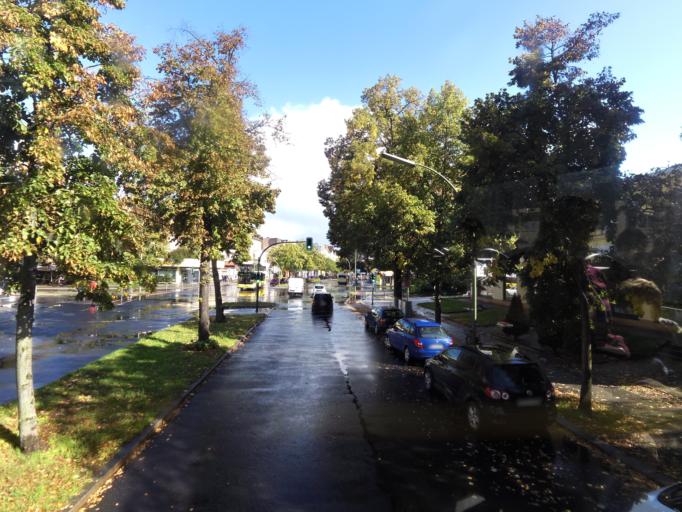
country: DE
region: Berlin
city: Schmargendorf
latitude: 52.4755
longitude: 13.2895
